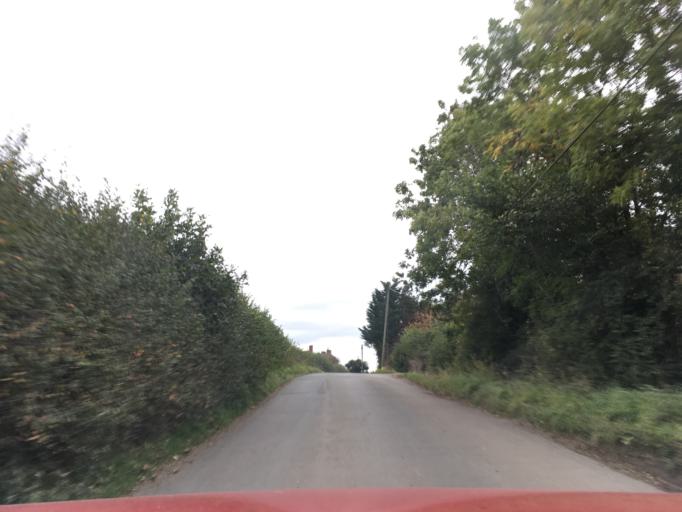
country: GB
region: England
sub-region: Gloucestershire
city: Stonehouse
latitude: 51.7583
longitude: -2.3103
